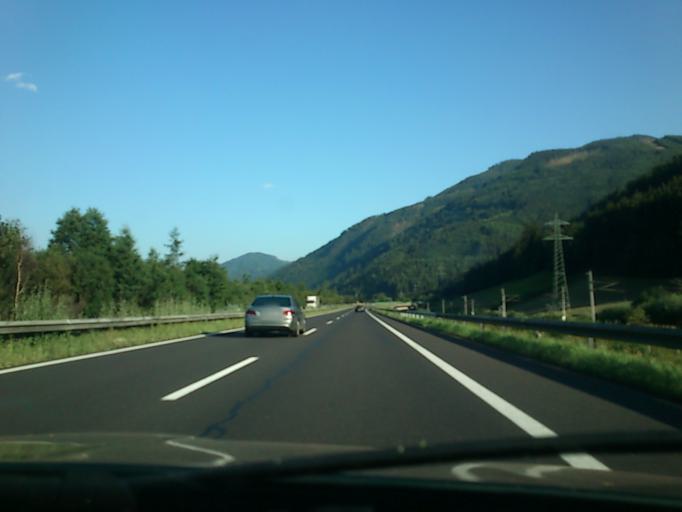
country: AT
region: Styria
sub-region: Politischer Bezirk Leoben
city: Kalwang
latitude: 47.4149
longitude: 14.7671
